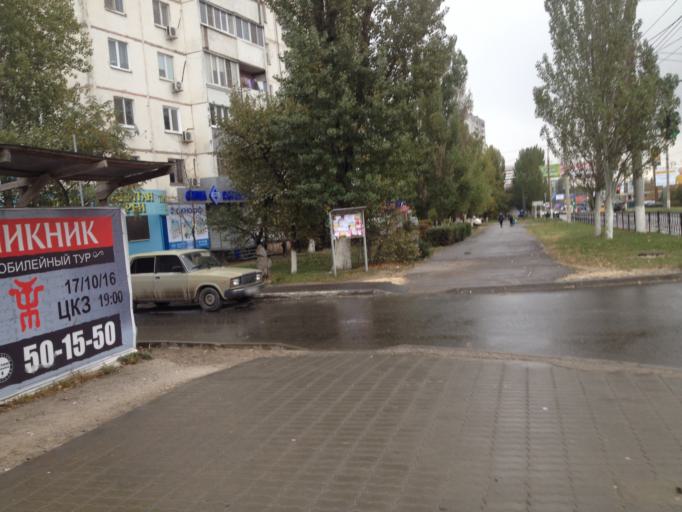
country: RU
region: Volgograd
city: Volgograd
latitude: 48.7499
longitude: 44.4984
